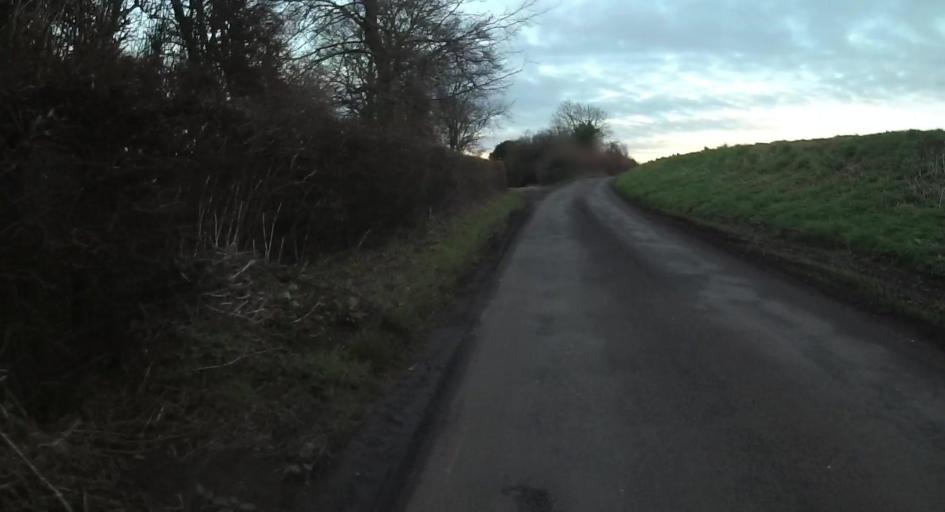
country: GB
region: England
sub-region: Hampshire
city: Swanmore
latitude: 51.0144
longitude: -1.1431
